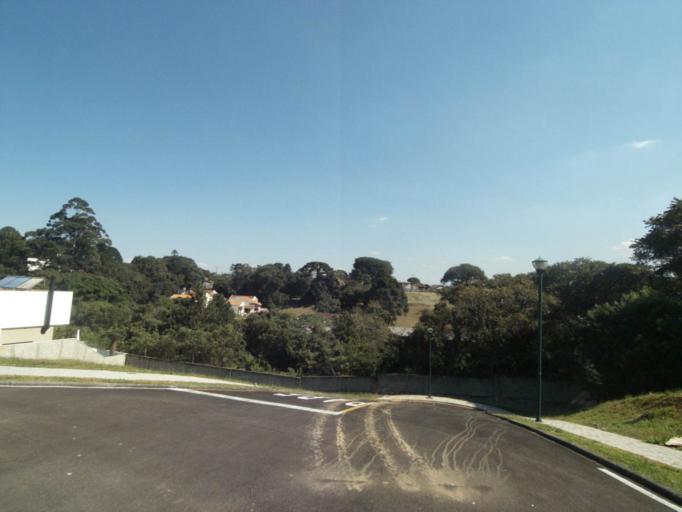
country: BR
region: Parana
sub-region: Curitiba
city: Curitiba
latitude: -25.3833
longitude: -49.2838
